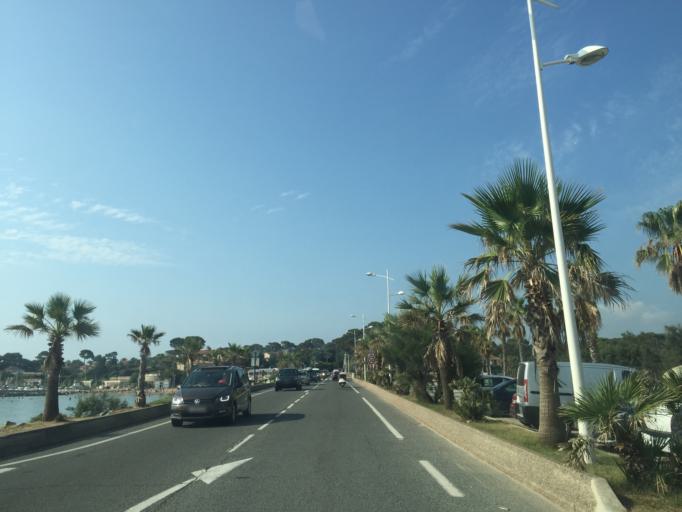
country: FR
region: Provence-Alpes-Cote d'Azur
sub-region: Departement du Var
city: Frejus
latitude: 43.3947
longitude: 6.7284
